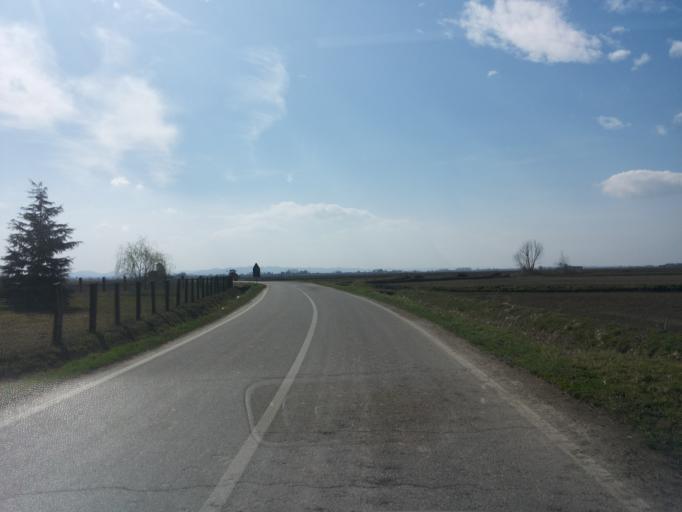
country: IT
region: Piedmont
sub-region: Provincia di Vercelli
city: Asigliano Vercellese
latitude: 45.2572
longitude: 8.3994
